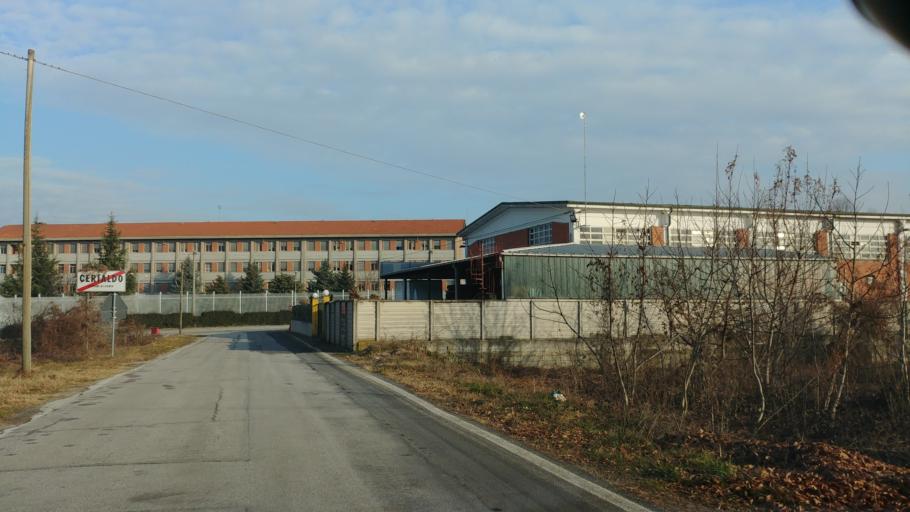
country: IT
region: Piedmont
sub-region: Provincia di Cuneo
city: Cuneo
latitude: 44.4025
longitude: 7.5356
